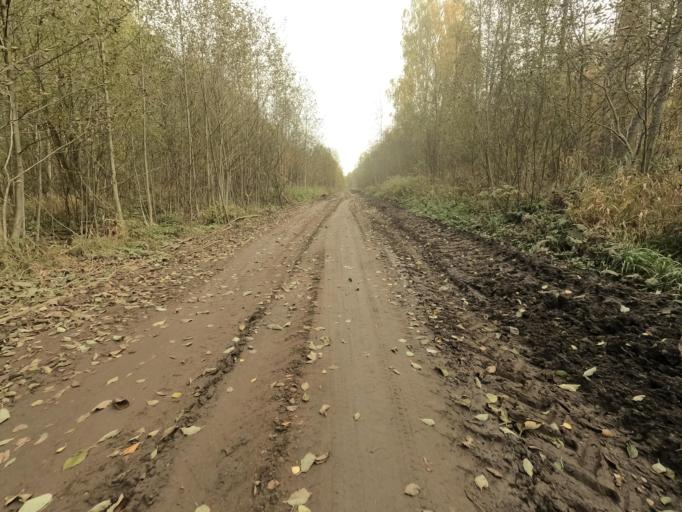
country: RU
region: Novgorod
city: Batetskiy
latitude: 58.8793
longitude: 30.7693
